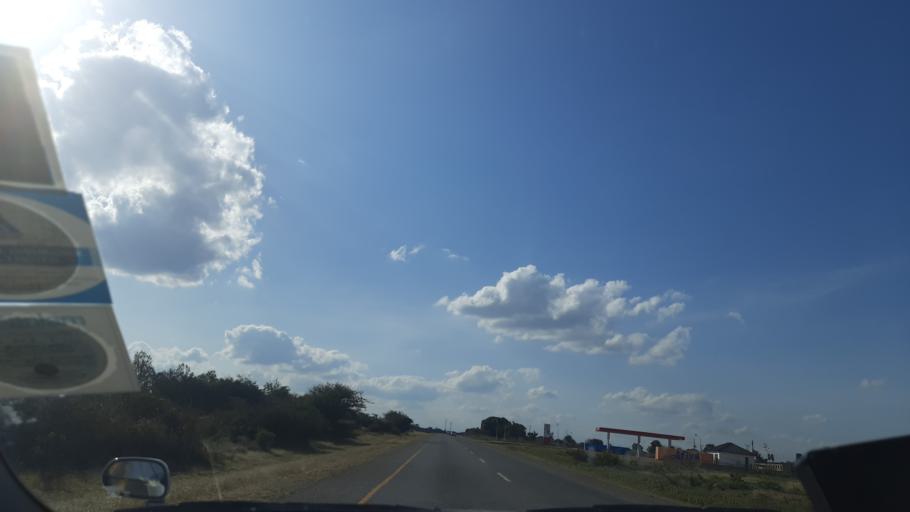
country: TZ
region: Singida
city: Ikungi
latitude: -5.1594
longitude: 34.7776
